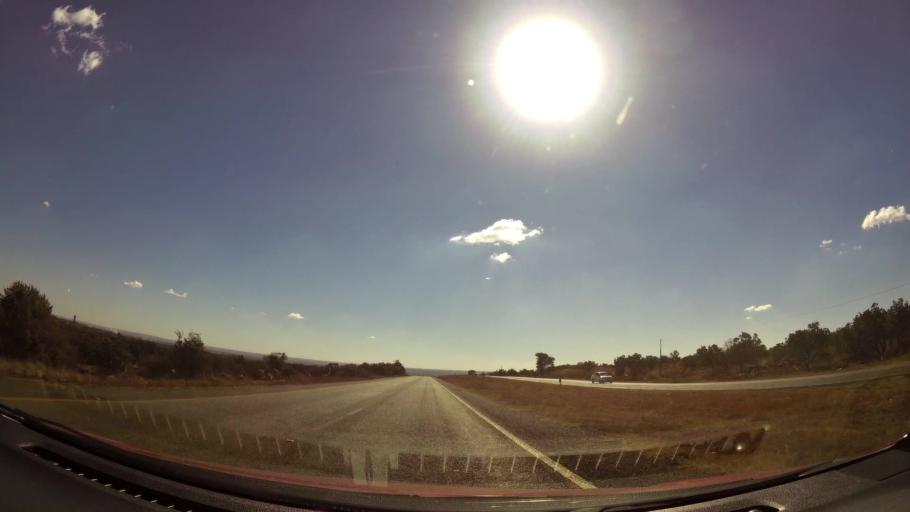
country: ZA
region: Gauteng
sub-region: West Rand District Municipality
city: Carletonville
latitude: -26.3858
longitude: 27.4133
